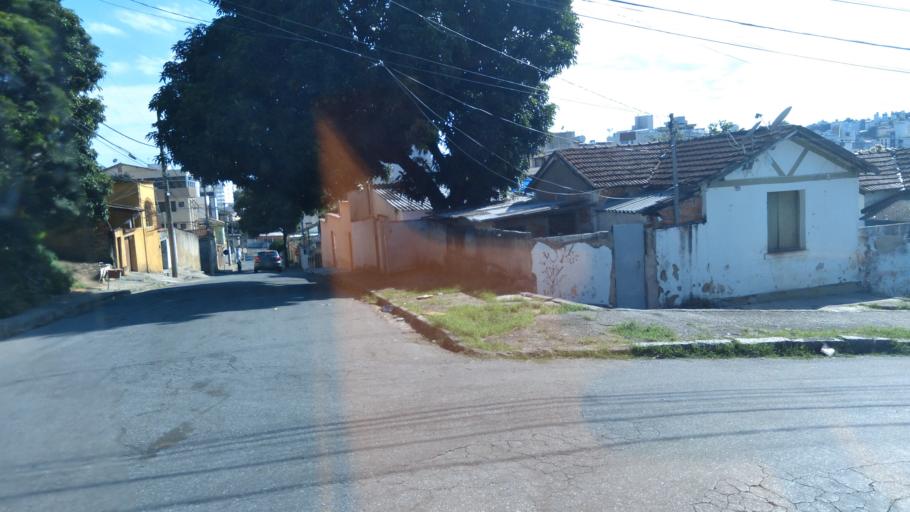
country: BR
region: Minas Gerais
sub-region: Belo Horizonte
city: Belo Horizonte
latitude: -19.8837
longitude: -43.9316
